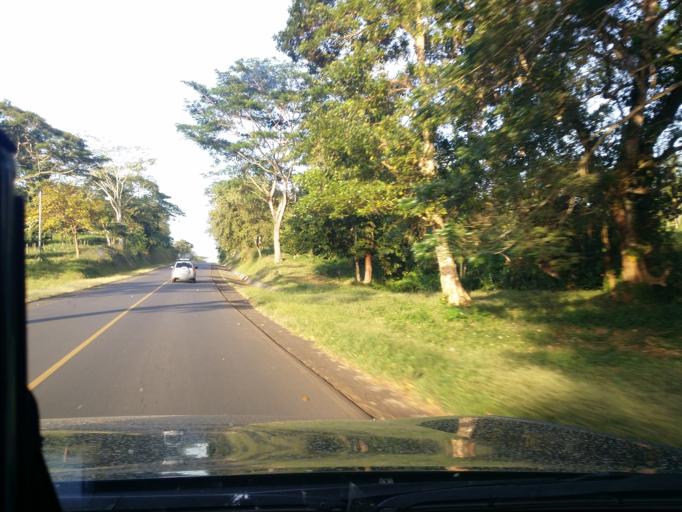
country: NI
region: Rio San Juan
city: San Miguelito
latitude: 11.4872
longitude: -84.8444
